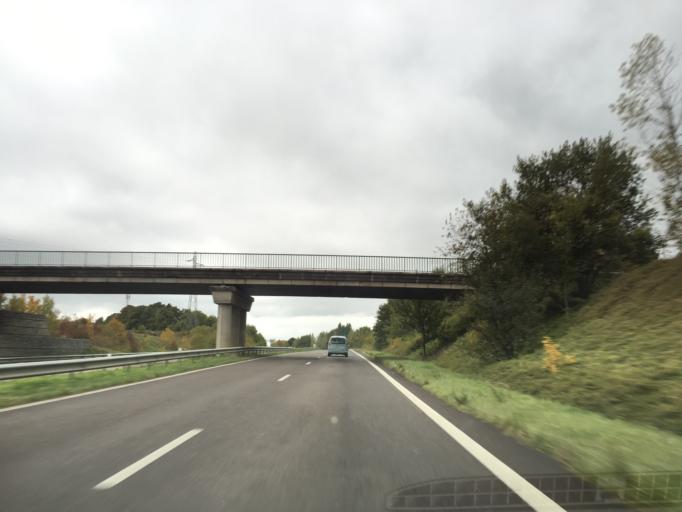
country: FR
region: Lorraine
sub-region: Departement de la Meuse
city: Euville
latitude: 48.6901
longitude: 5.6773
